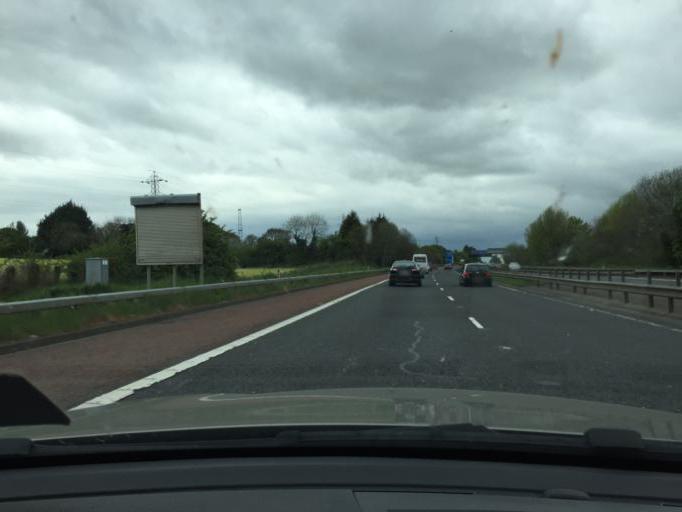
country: GB
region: Northern Ireland
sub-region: Lisburn District
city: Lisburn
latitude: 54.4960
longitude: -6.0473
